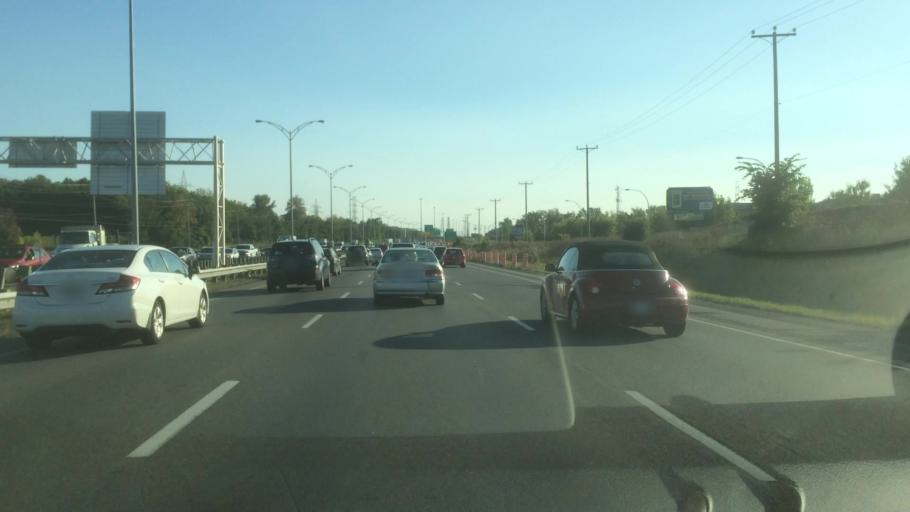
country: CA
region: Quebec
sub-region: Laurentides
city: Boisbriand
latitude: 45.6096
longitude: -73.8551
